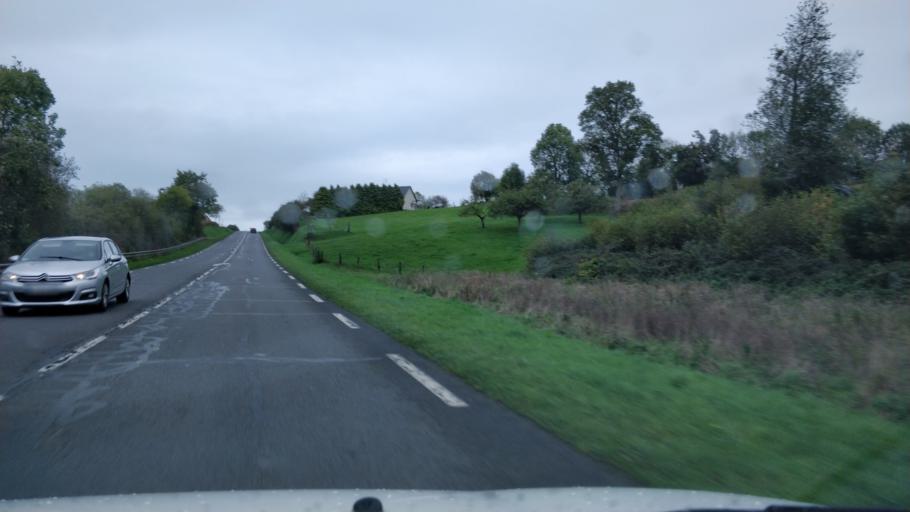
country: FR
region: Lower Normandy
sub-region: Departement de la Manche
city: Sartilly
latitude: 48.7764
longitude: -1.4903
